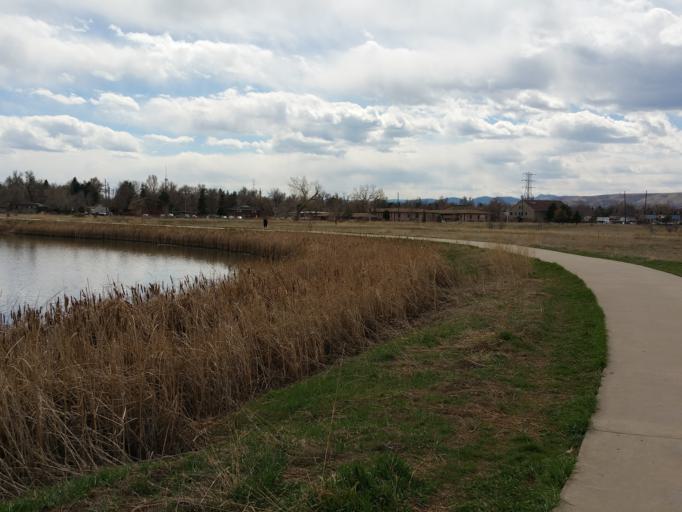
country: US
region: Colorado
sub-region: Jefferson County
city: Wheat Ridge
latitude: 39.7575
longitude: -105.1068
